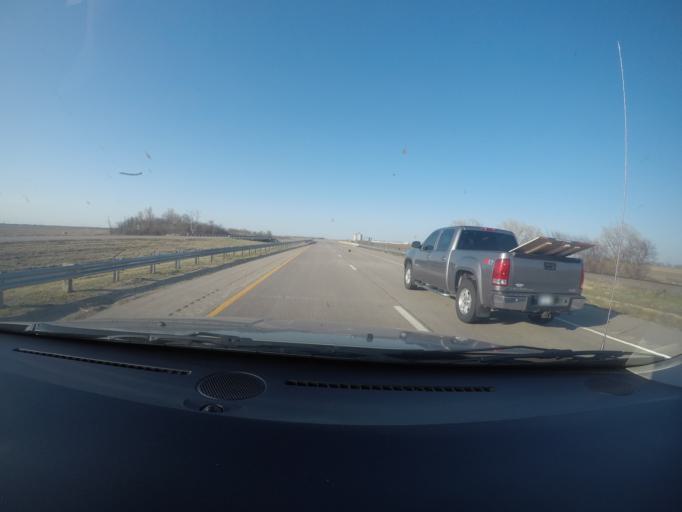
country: US
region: Kansas
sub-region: McPherson County
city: Inman
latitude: 38.2814
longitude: -97.7403
